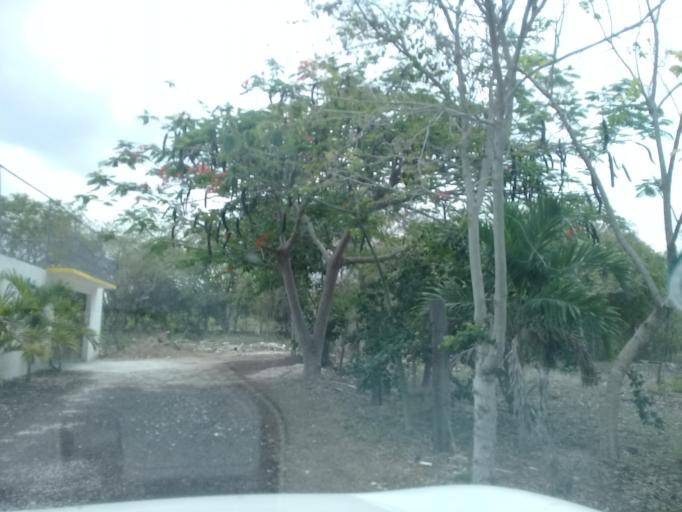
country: MX
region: Veracruz
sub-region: Emiliano Zapata
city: Plan del Rio
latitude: 19.3553
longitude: -96.6590
